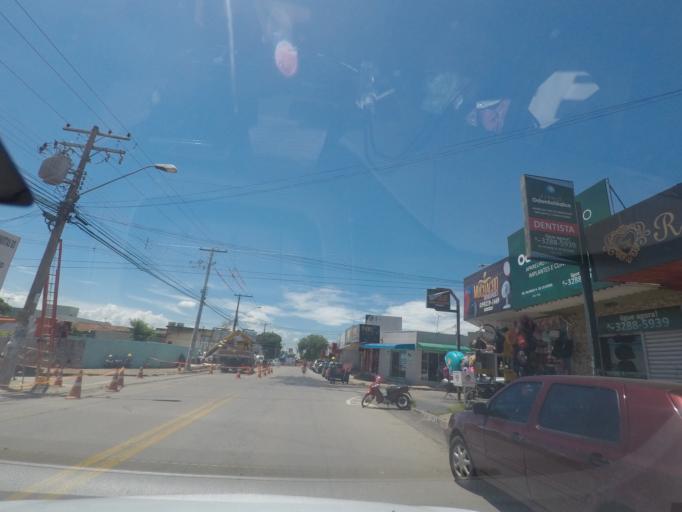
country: BR
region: Goias
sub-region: Aparecida De Goiania
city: Aparecida de Goiania
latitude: -16.7675
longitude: -49.3432
